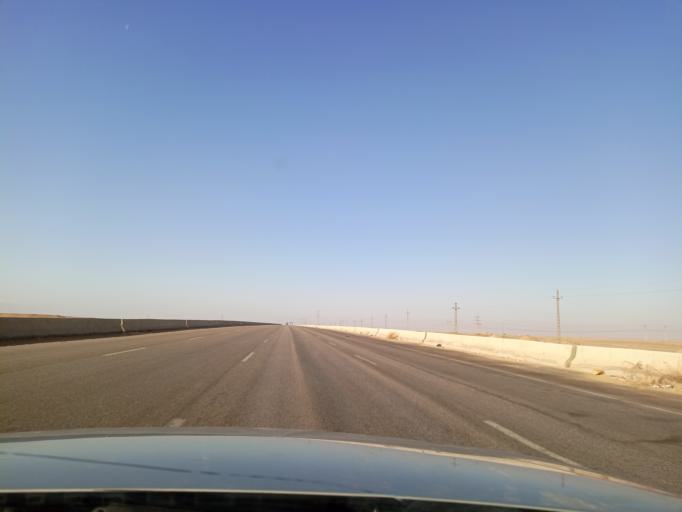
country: EG
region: Muhafazat al Fayyum
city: Tamiyah
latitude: 29.6358
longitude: 30.9820
